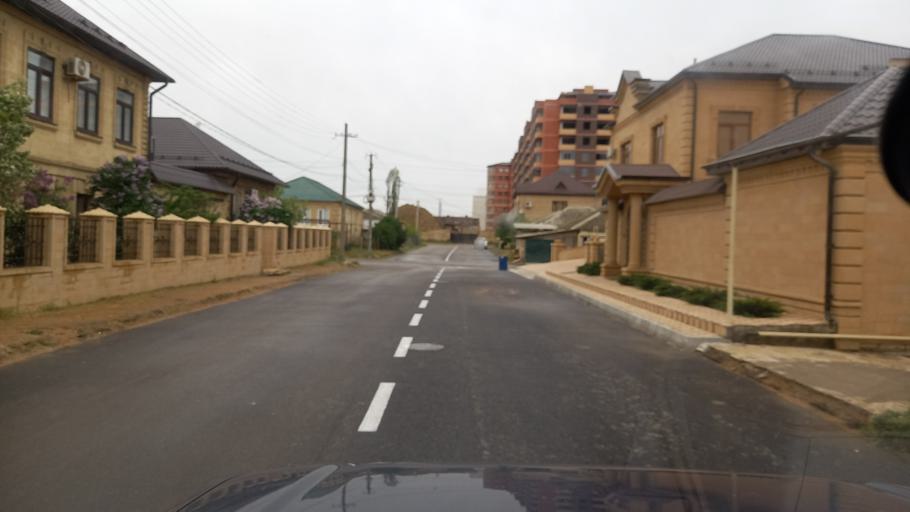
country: RU
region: Dagestan
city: Derbent
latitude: 42.0819
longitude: 48.2931
